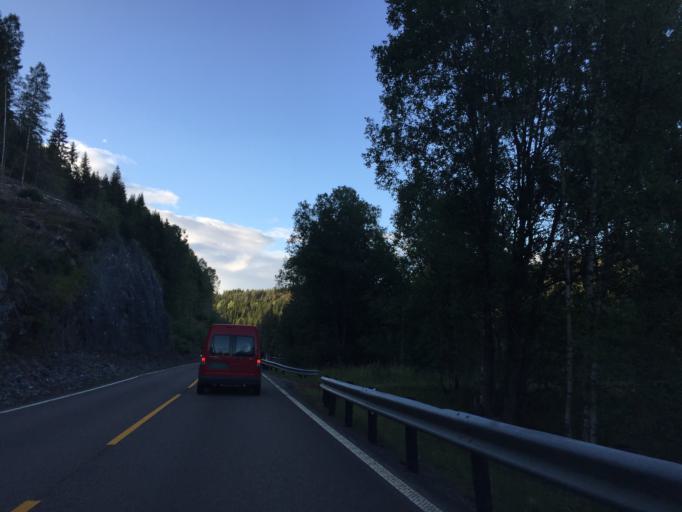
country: NO
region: Akershus
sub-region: Enebakk
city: Flateby
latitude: 59.8390
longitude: 11.2474
